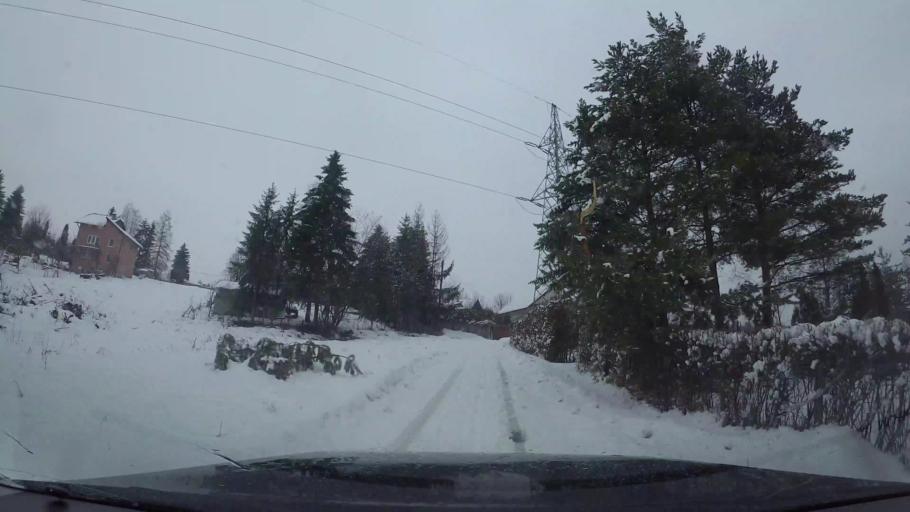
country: BA
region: Federation of Bosnia and Herzegovina
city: Hadzici
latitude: 43.8608
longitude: 18.2631
